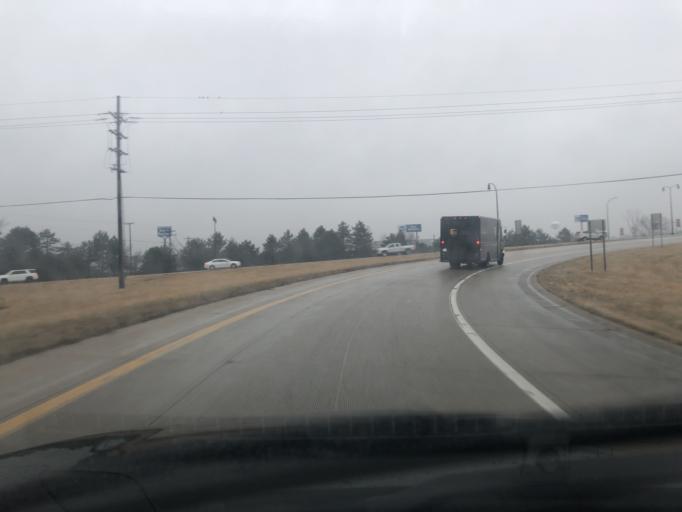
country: US
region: Michigan
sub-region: Wayne County
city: Woodhaven
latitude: 42.1378
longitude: -83.2437
